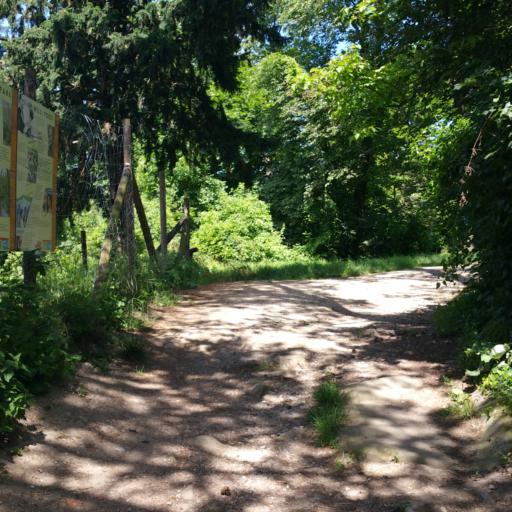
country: AT
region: Lower Austria
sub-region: Politischer Bezirk Modling
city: Perchtoldsdorf
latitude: 48.2062
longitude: 16.2667
